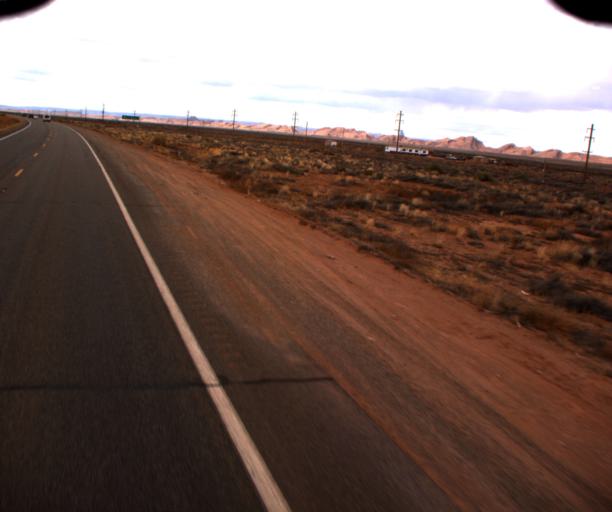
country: US
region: Arizona
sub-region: Navajo County
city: Kayenta
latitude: 36.7769
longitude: -110.0110
